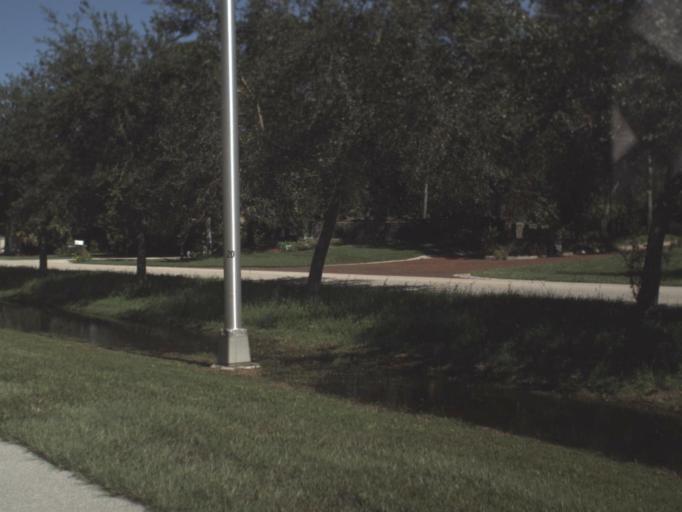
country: US
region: Florida
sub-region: Collier County
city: Pine Ridge
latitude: 26.2182
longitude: -81.8004
